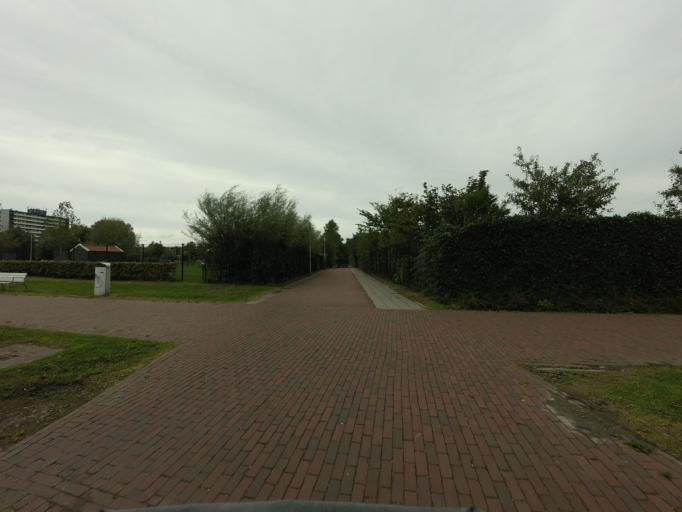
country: NL
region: Friesland
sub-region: Gemeente Leeuwarden
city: Bilgaard
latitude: 53.2118
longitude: 5.7931
